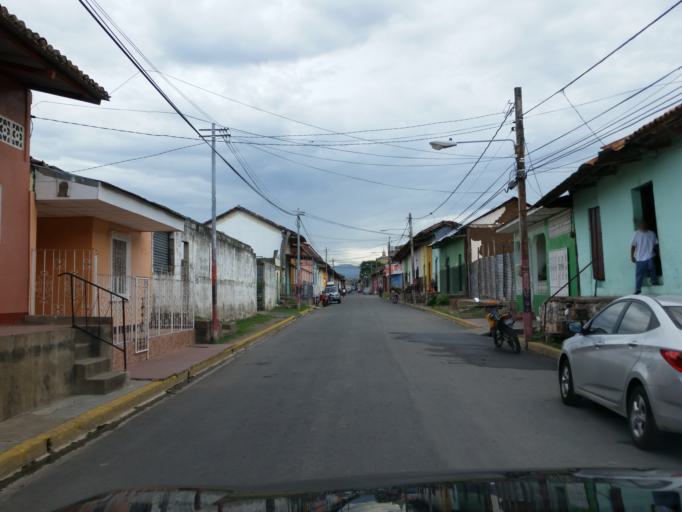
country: NI
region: Granada
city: Granada
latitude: 11.9319
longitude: -85.9492
